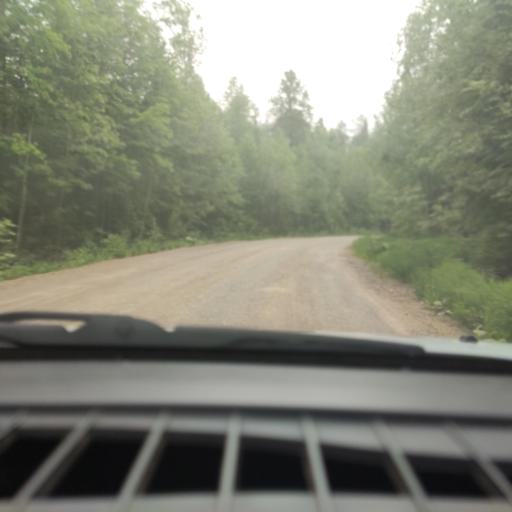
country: RU
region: Perm
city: Novyye Lyady
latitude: 57.8998
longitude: 56.6524
